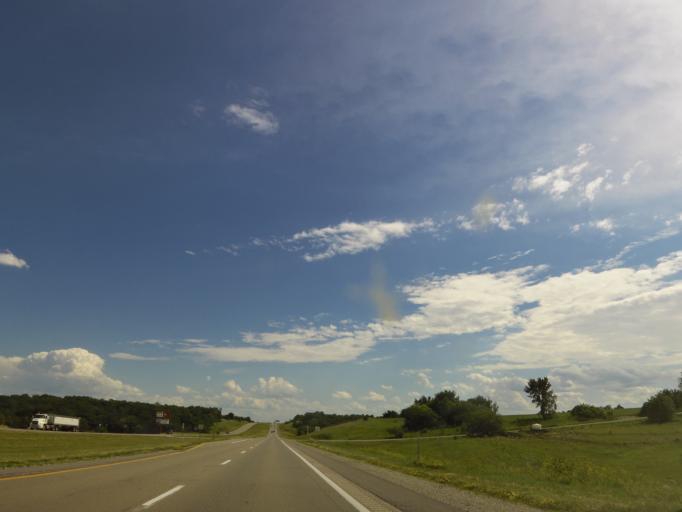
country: US
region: Iowa
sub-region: Henry County
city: Winfield
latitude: 41.2081
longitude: -91.5292
